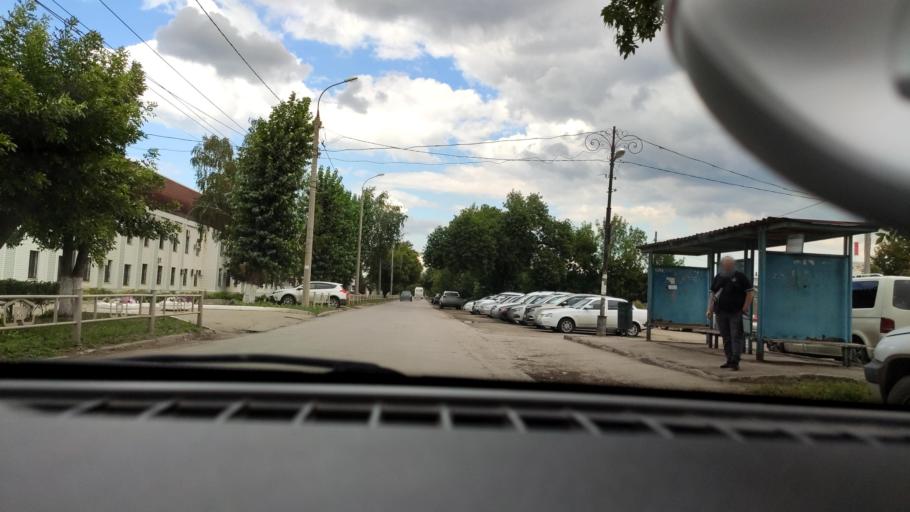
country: RU
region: Samara
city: Novokuybyshevsk
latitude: 53.1045
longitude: 50.0381
